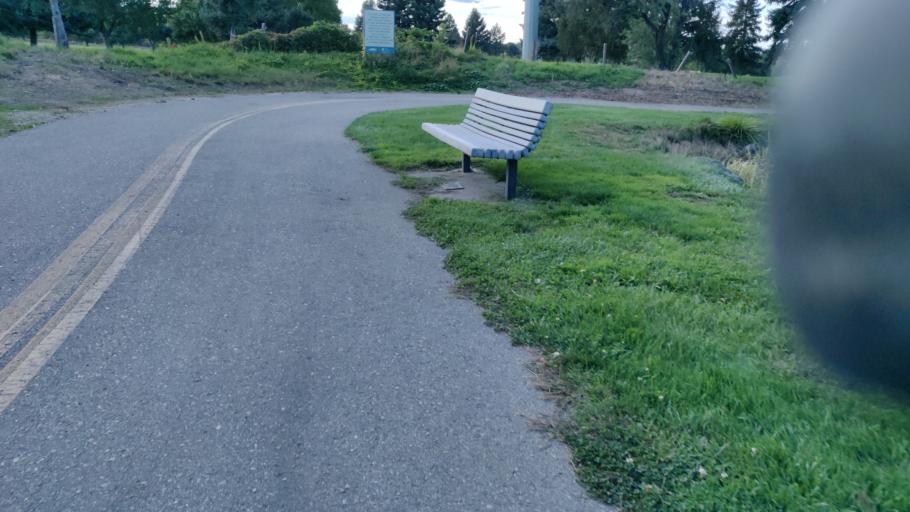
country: US
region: Idaho
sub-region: Ada County
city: Boise
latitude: 43.5975
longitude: -116.1701
